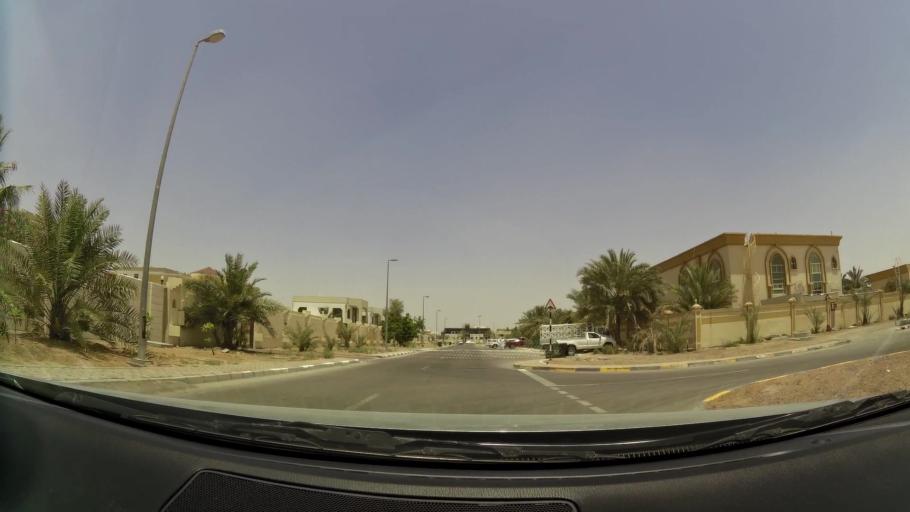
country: OM
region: Al Buraimi
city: Al Buraymi
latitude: 24.2617
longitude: 55.7181
